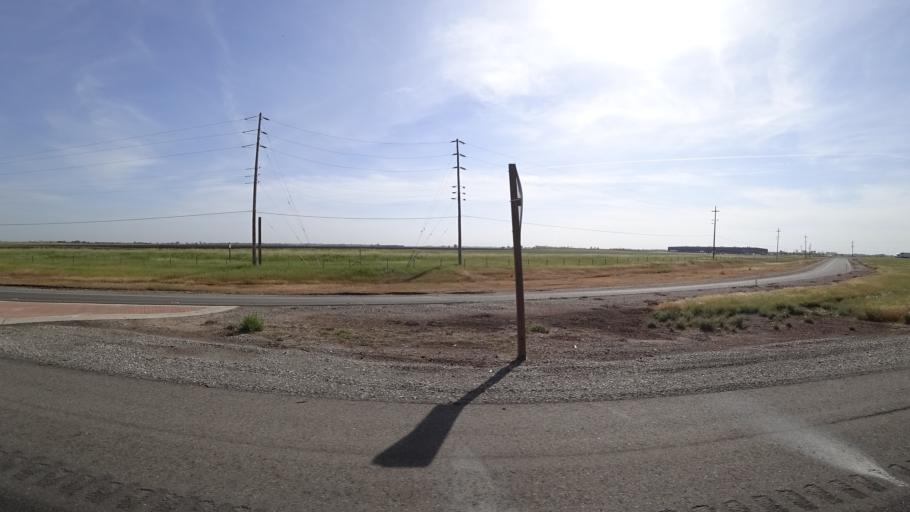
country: US
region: California
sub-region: Butte County
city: Durham
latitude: 39.6407
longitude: -121.7145
